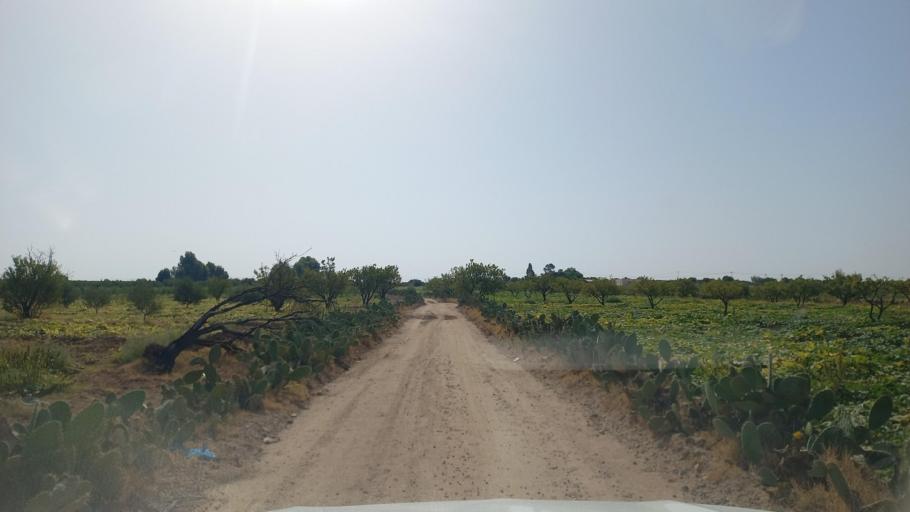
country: TN
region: Al Qasrayn
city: Kasserine
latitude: 35.2466
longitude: 9.0385
